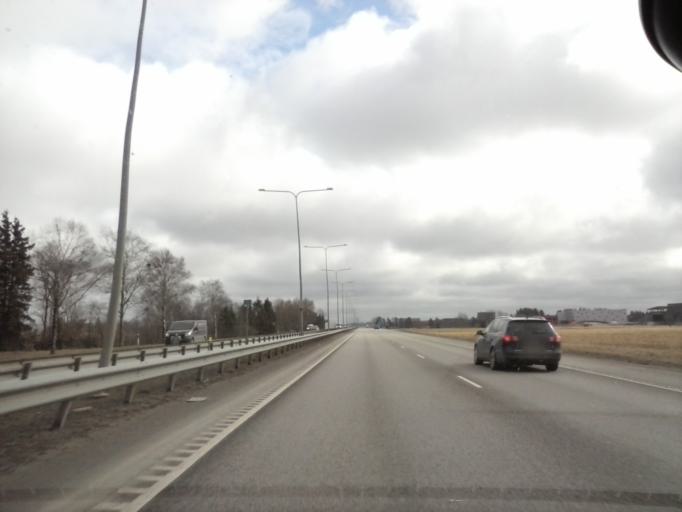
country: EE
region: Harju
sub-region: Rae vald
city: Jueri
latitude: 59.3912
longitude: 24.8268
